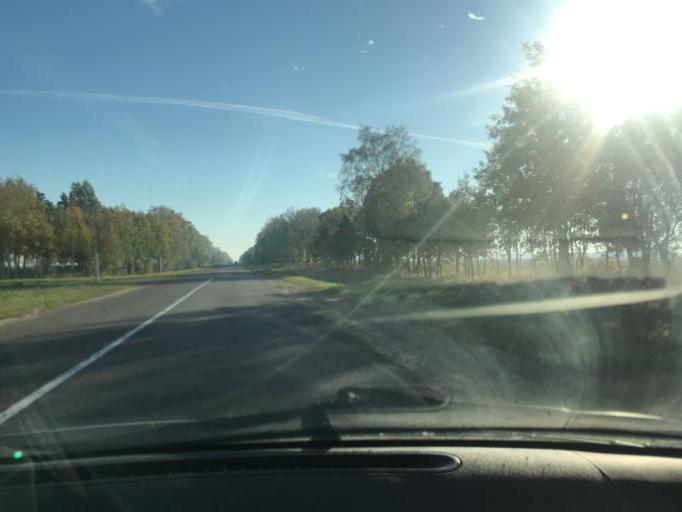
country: BY
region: Brest
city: Ivanava
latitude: 52.1459
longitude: 25.4664
